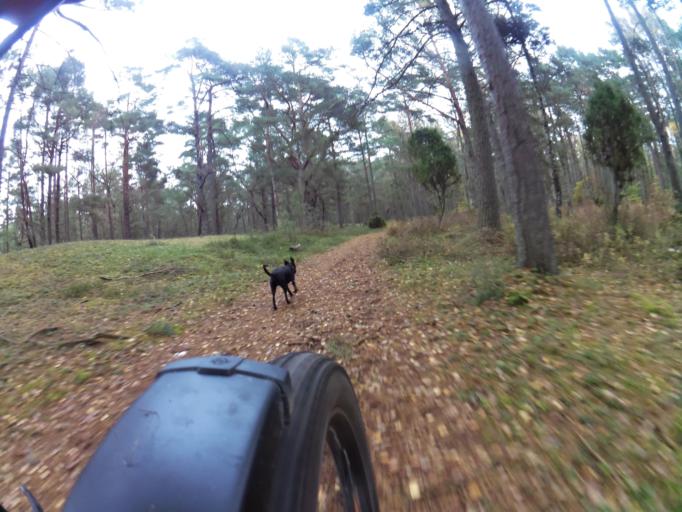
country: PL
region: Pomeranian Voivodeship
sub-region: Powiat leborski
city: Leba
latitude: 54.7755
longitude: 17.6761
